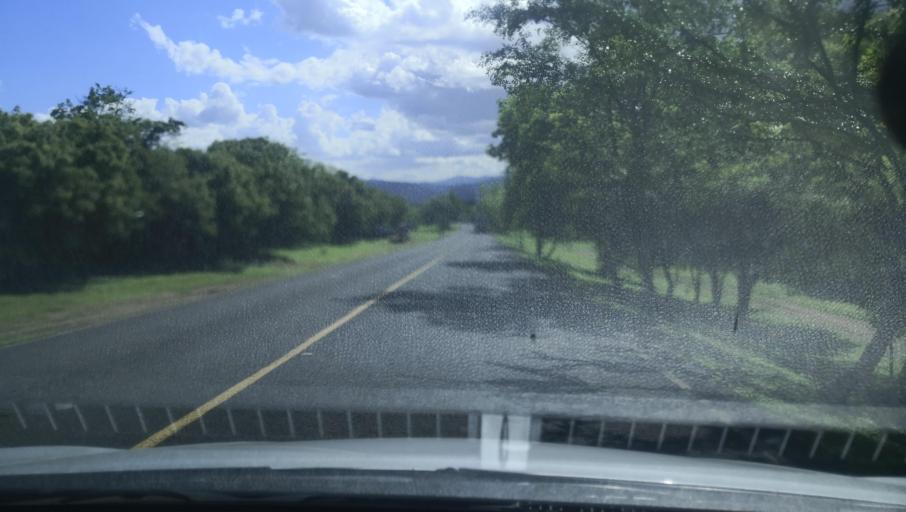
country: NI
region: Madriz
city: Somoto
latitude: 13.4722
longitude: -86.6184
